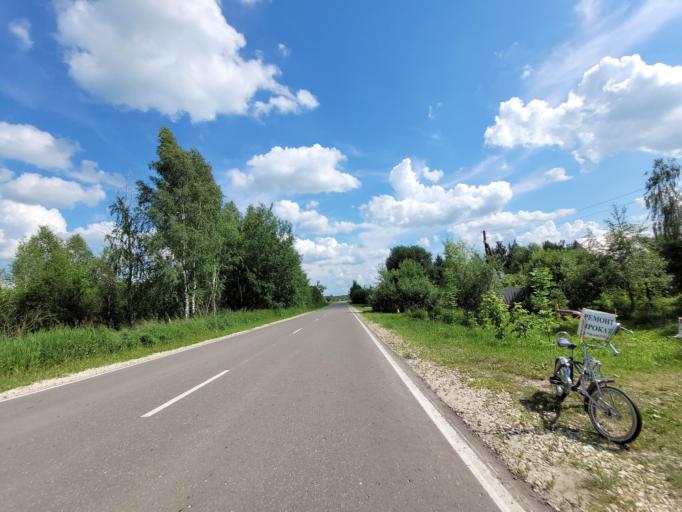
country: RU
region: Moskovskaya
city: Konobeyevo
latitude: 55.3969
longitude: 38.6824
